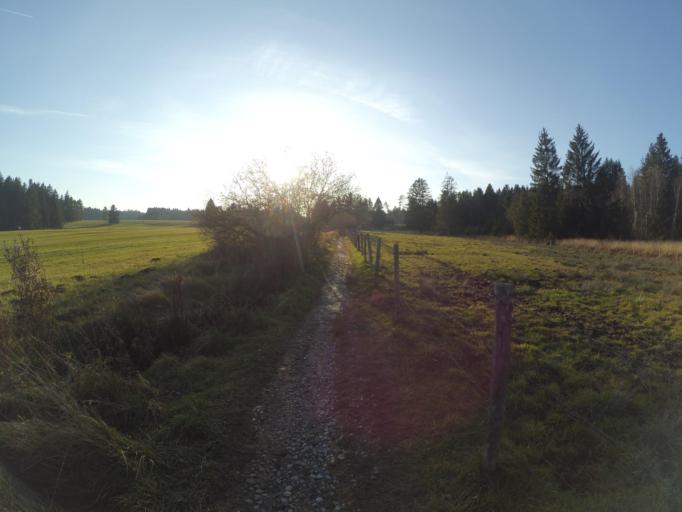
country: DE
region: Bavaria
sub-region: Swabia
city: Aitrang
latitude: 47.7942
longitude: 10.5414
